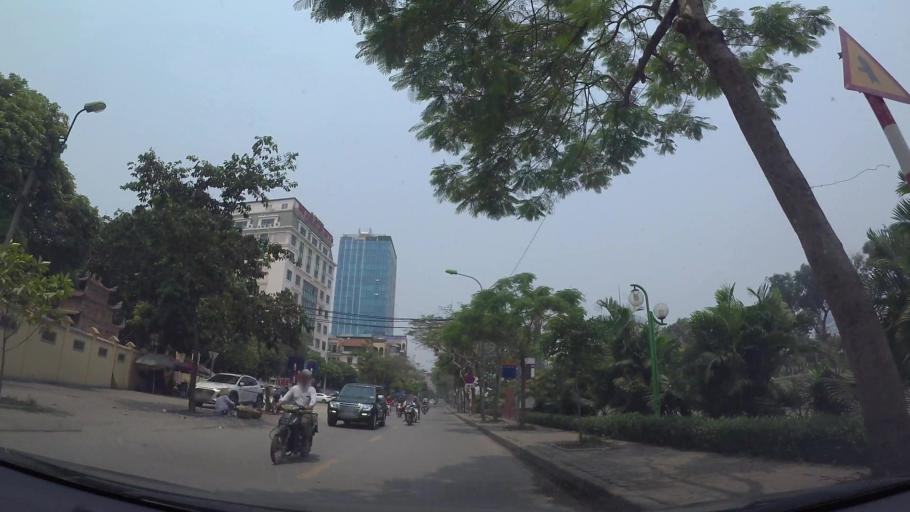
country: VN
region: Ha Noi
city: Thanh Xuan
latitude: 21.0112
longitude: 105.8093
